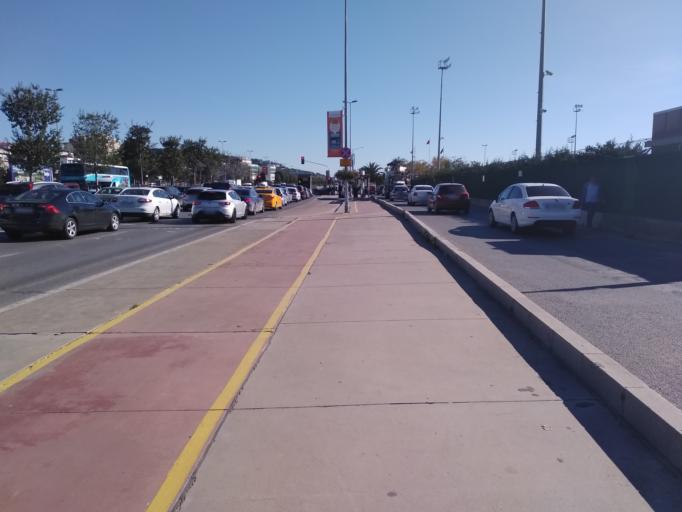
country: TR
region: Istanbul
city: Maltepe
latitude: 40.9185
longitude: 29.1294
